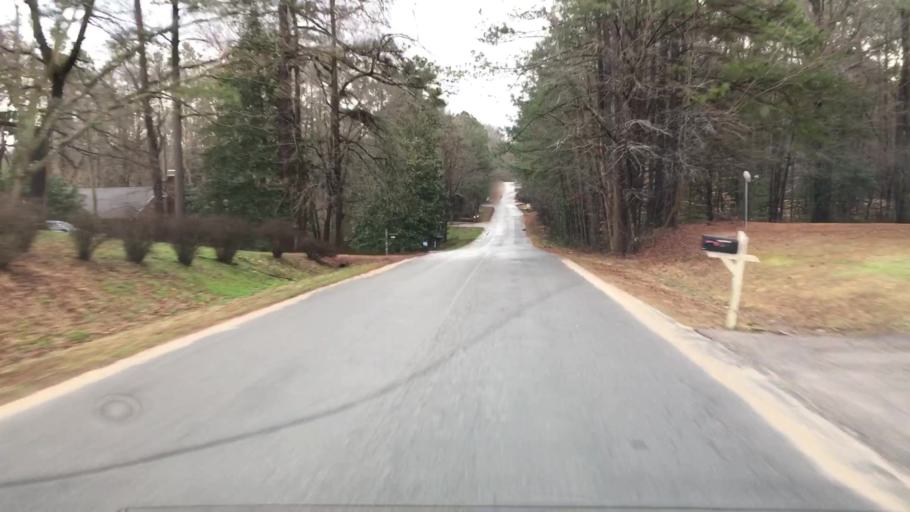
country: US
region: Virginia
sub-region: Chesterfield County
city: Bon Air
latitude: 37.4759
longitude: -77.5929
